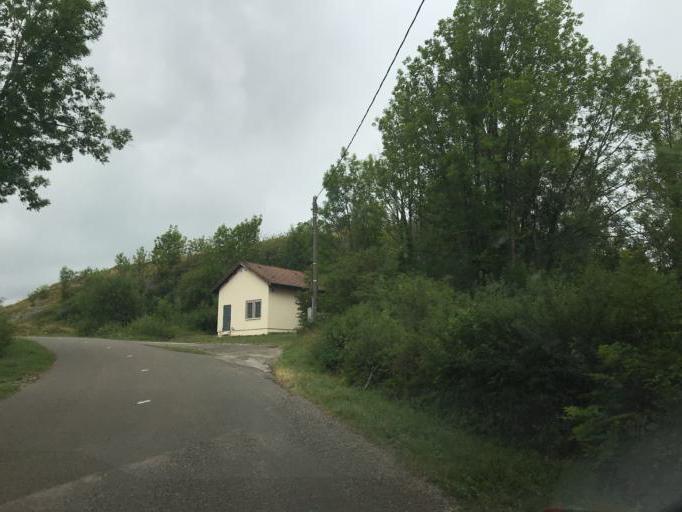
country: FR
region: Rhone-Alpes
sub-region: Departement de l'Ain
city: Arbent
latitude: 46.3040
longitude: 5.7431
